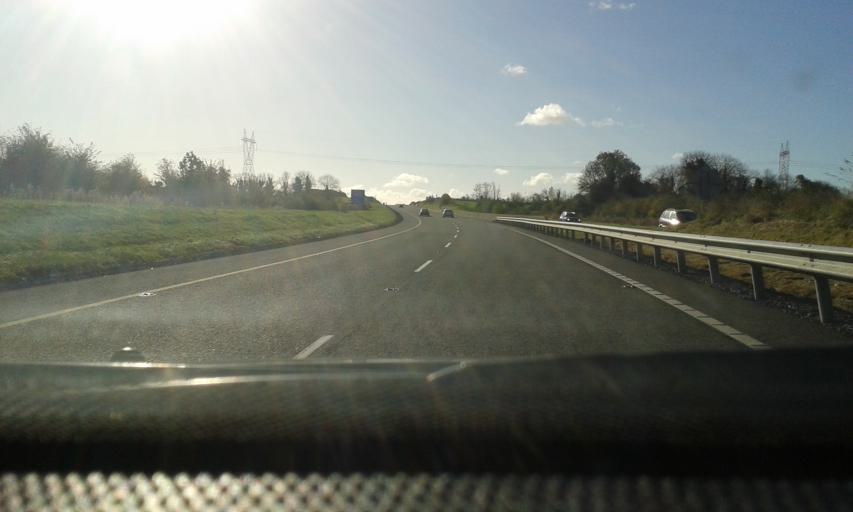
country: IE
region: Leinster
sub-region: Laois
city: Mountrath
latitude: 52.9161
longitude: -7.4867
